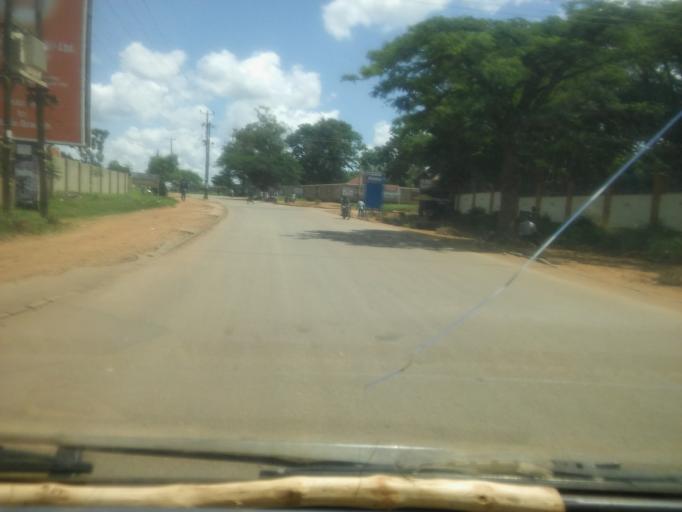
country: UG
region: Eastern Region
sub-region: Mbale District
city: Mbale
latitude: 1.0790
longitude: 34.1713
